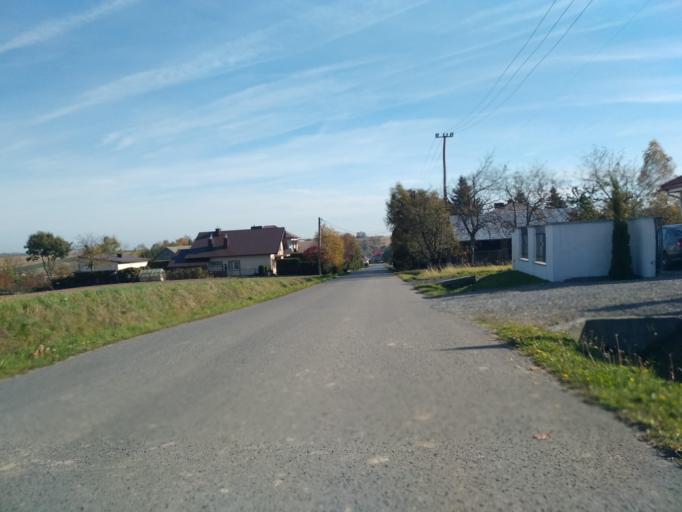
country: PL
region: Subcarpathian Voivodeship
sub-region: Powiat ropczycko-sedziszowski
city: Iwierzyce
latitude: 50.0051
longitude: 21.7506
